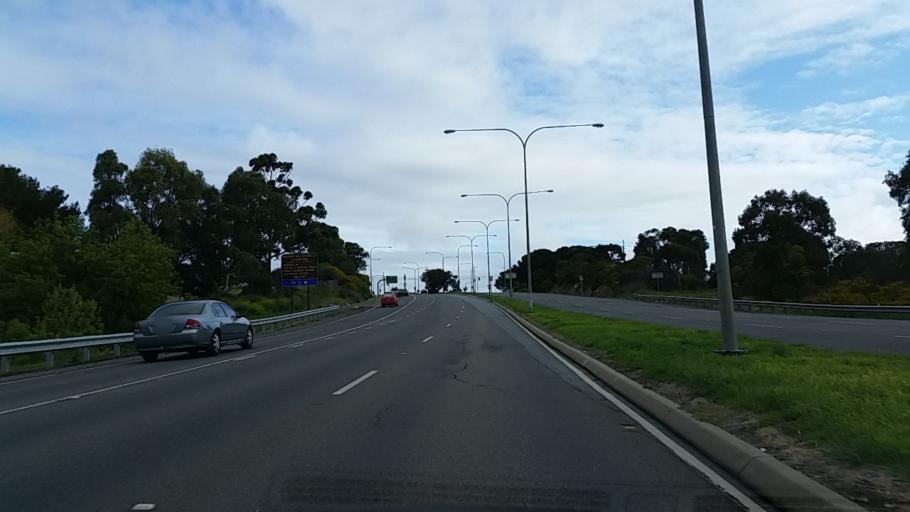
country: AU
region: South Australia
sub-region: Marion
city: Trott Park
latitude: -35.0785
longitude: 138.5481
